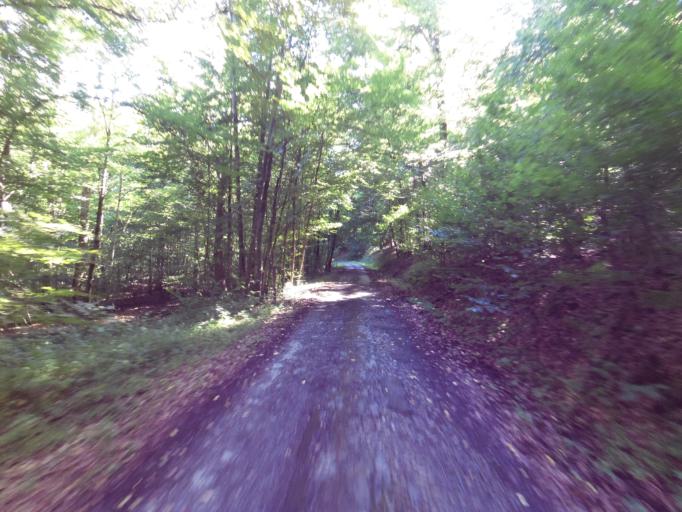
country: BE
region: Wallonia
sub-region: Province du Luxembourg
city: Nassogne
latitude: 50.0913
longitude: 5.3446
